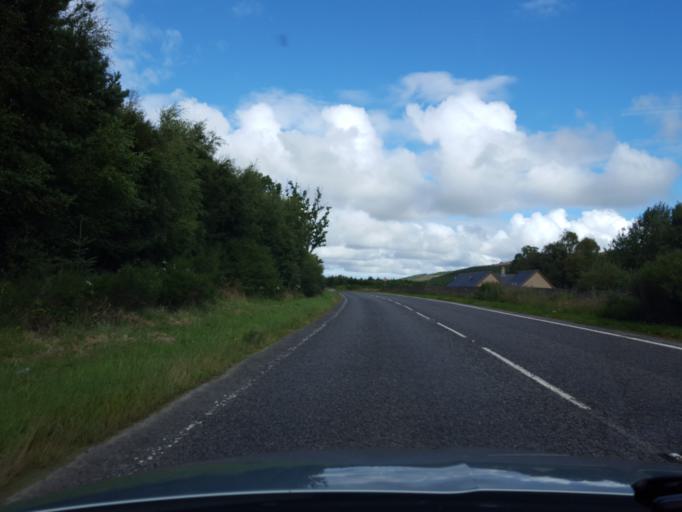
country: GB
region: Scotland
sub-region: Moray
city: Rothes
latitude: 57.5420
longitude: -3.2298
